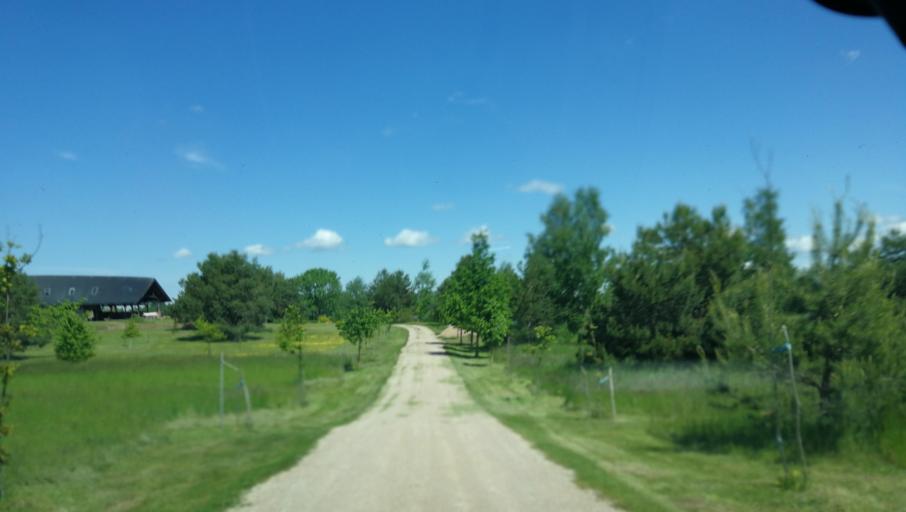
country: LV
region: Kekava
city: Kekava
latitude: 56.8759
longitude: 24.2067
